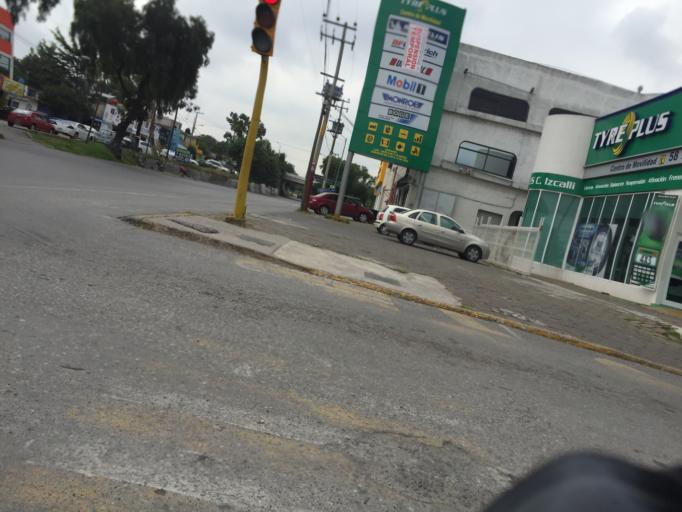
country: MX
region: Mexico
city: Cuautitlan Izcalli
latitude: 19.6601
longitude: -99.2076
